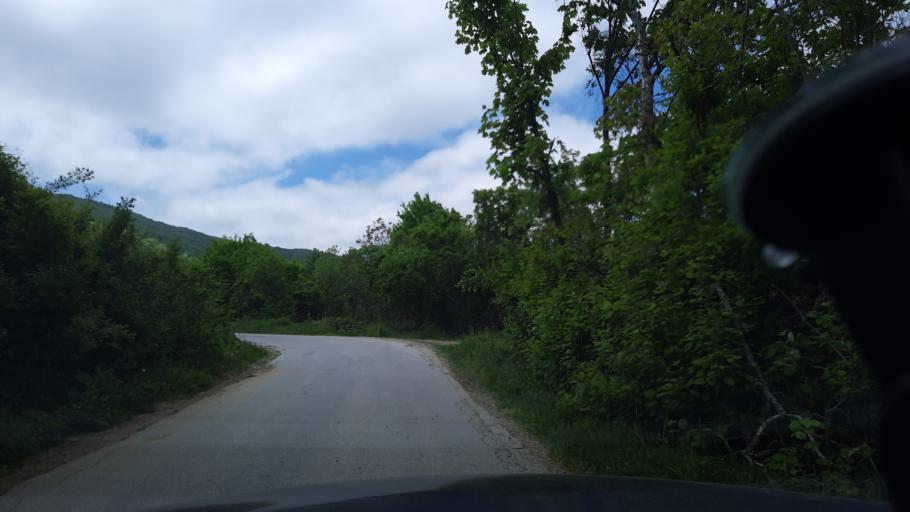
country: MK
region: Bitola
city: Bitola
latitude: 41.0296
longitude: 21.2890
